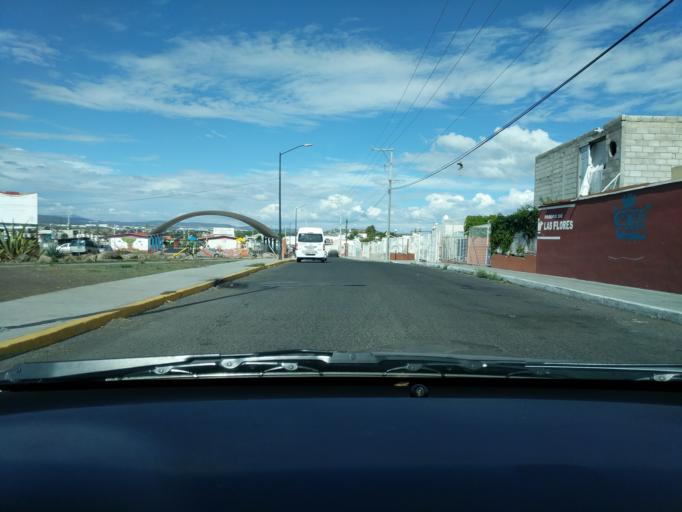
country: MX
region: Queretaro
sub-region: El Marques
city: Paseos del Marques
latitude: 20.6027
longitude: -100.2409
